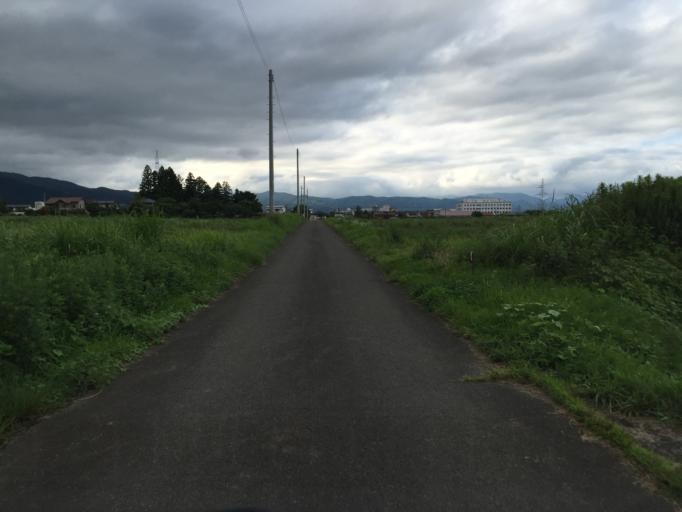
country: JP
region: Fukushima
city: Fukushima-shi
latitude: 37.7205
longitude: 140.3894
